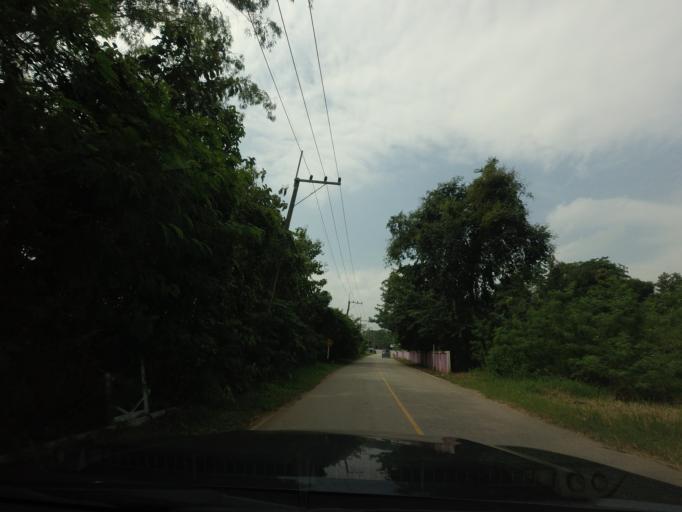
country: TH
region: Loei
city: Tha Li
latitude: 17.6637
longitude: 101.3550
